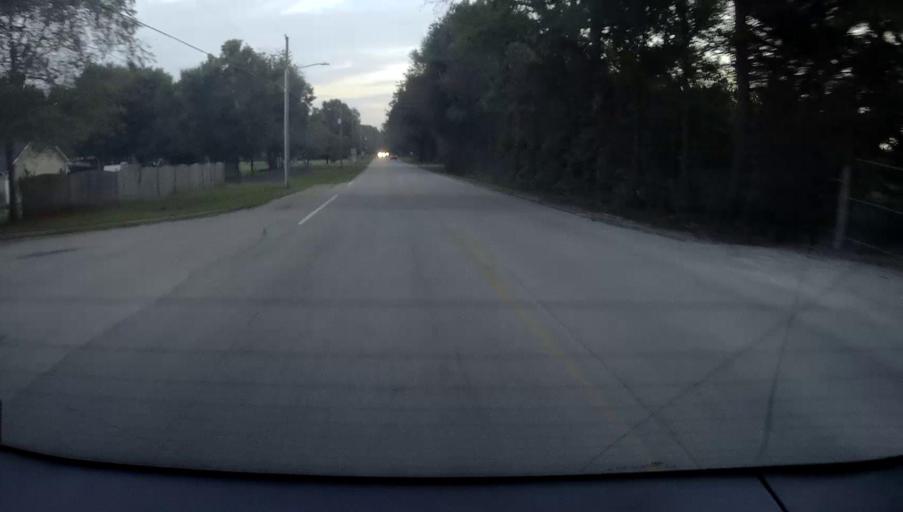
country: US
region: Georgia
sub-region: Henry County
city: Locust Grove
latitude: 33.3198
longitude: -84.0428
